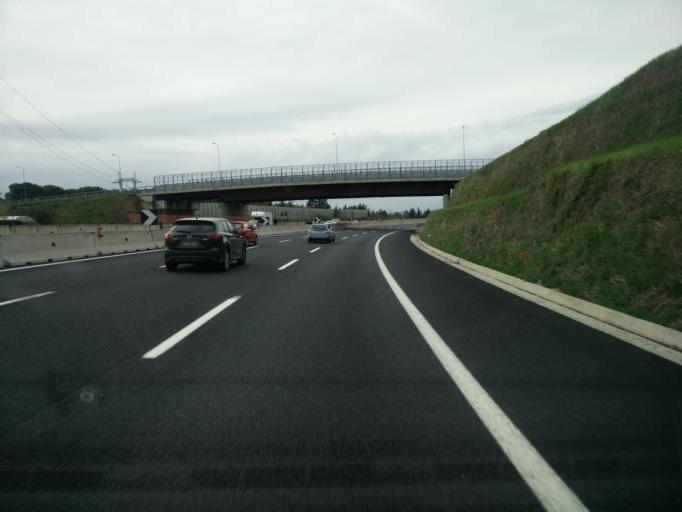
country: IT
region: Tuscany
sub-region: Province of Florence
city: Scandicci
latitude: 43.7461
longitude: 11.1738
